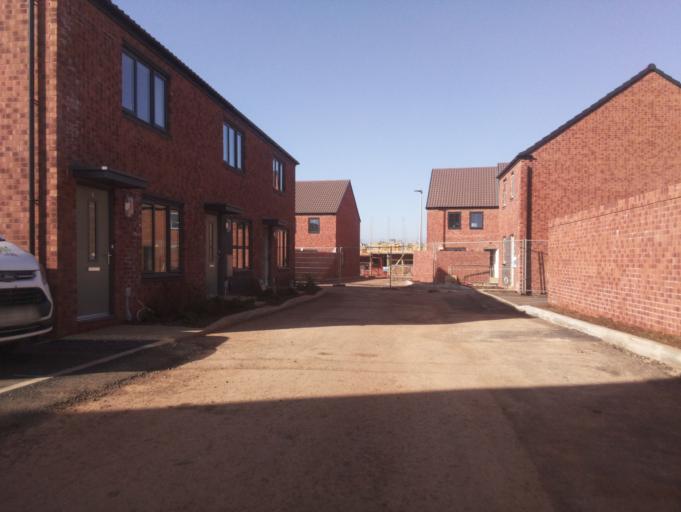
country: GB
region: England
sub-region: South Gloucestershire
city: Yate
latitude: 51.5601
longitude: -2.4219
